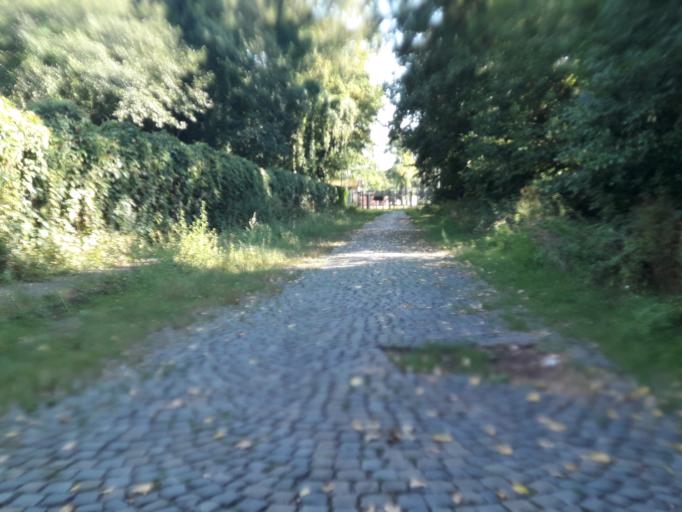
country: DE
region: North Rhine-Westphalia
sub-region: Regierungsbezirk Detmold
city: Paderborn
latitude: 51.7753
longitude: 8.7185
